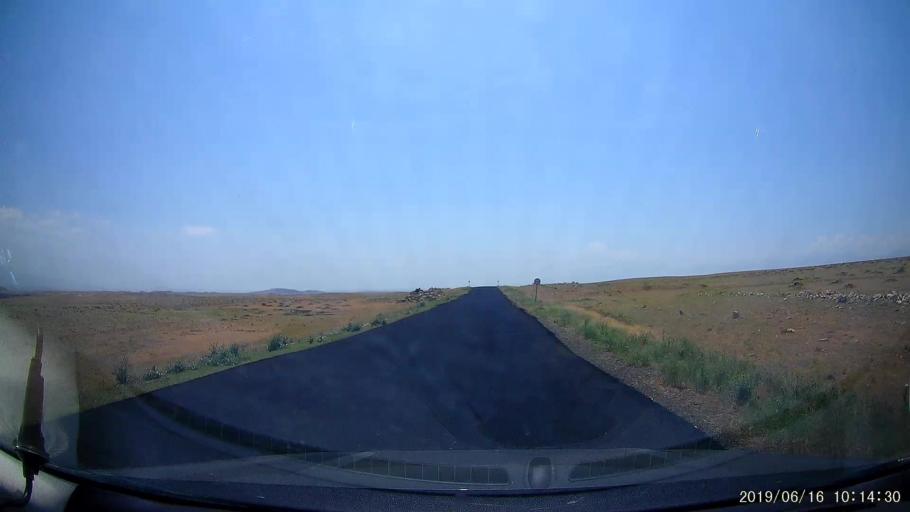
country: TR
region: Igdir
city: Tuzluca
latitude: 40.1841
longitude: 43.6644
